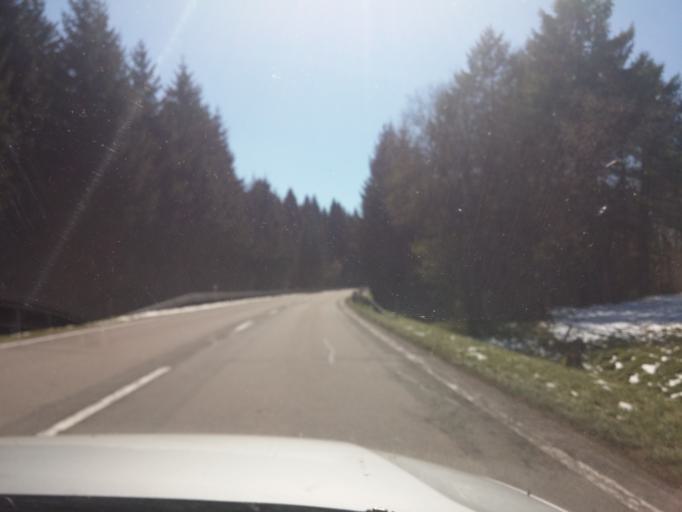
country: DE
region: Baden-Wuerttemberg
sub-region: Tuebingen Region
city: Bad Wurzach
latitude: 47.9209
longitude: 9.9767
